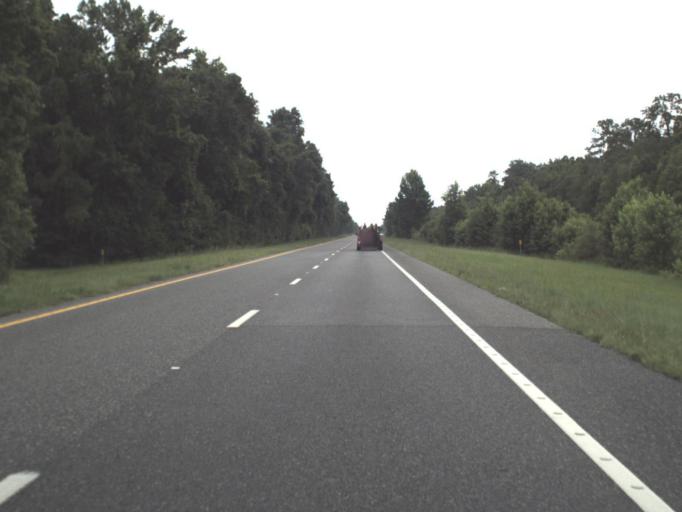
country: US
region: Florida
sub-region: Levy County
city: Bronson
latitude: 29.2660
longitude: -82.7309
